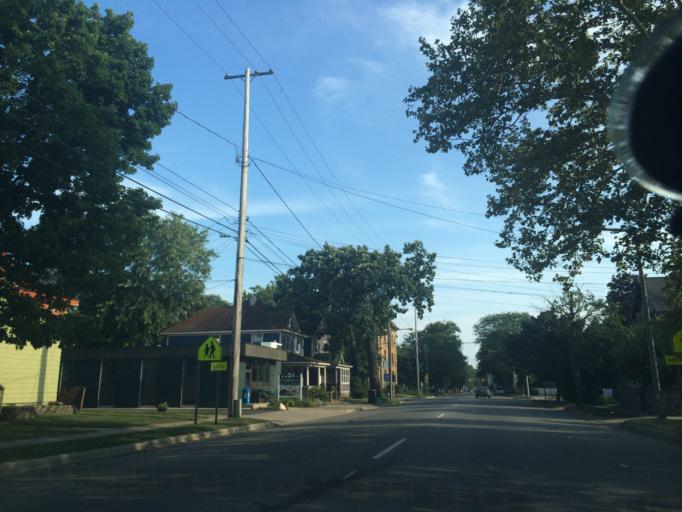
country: US
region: Michigan
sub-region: Kalamazoo County
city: Kalamazoo
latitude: 42.2870
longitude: -85.5895
